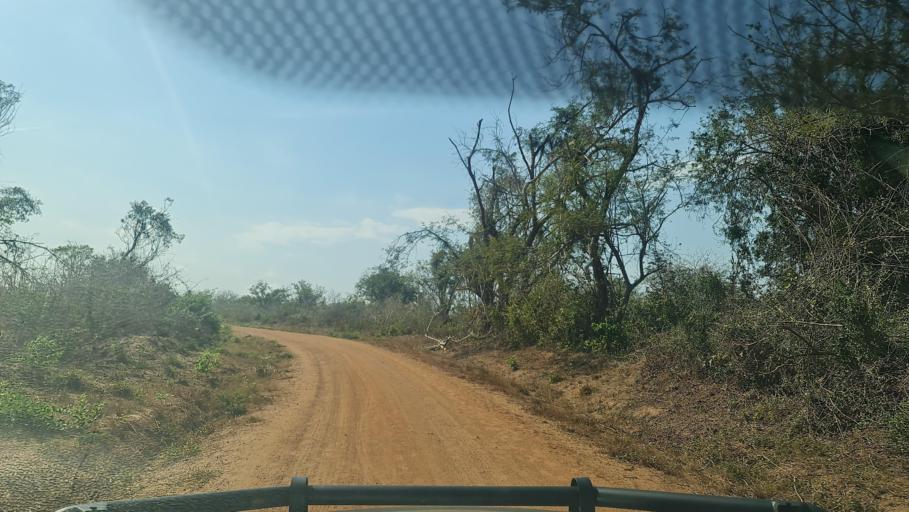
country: MZ
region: Nampula
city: Ilha de Mocambique
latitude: -15.1306
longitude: 40.2140
